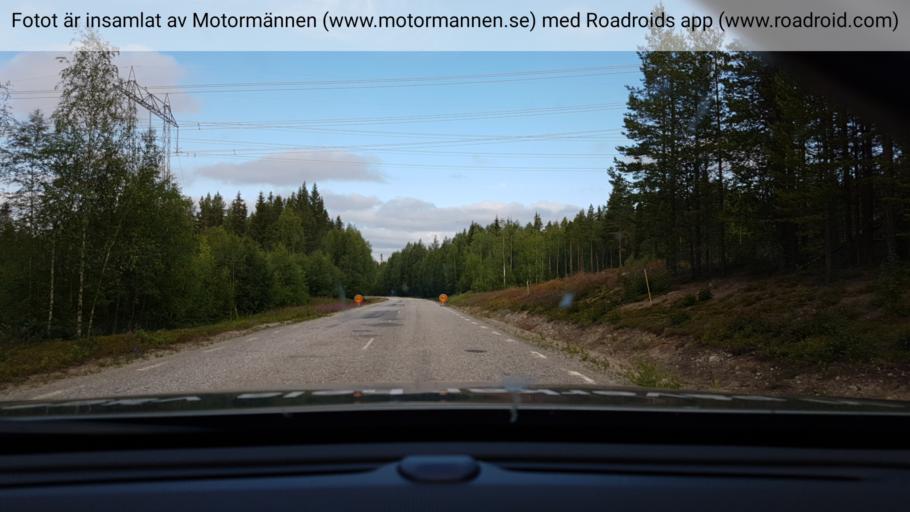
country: SE
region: Vaesterbotten
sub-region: Norsjo Kommun
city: Norsjoe
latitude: 64.6885
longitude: 19.2157
